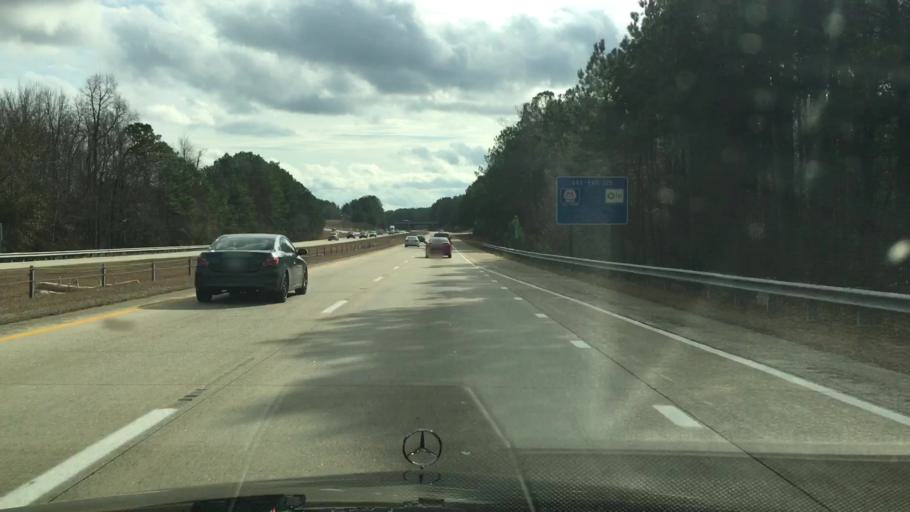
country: US
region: North Carolina
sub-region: Johnston County
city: Benson
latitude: 35.4293
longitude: -78.5320
